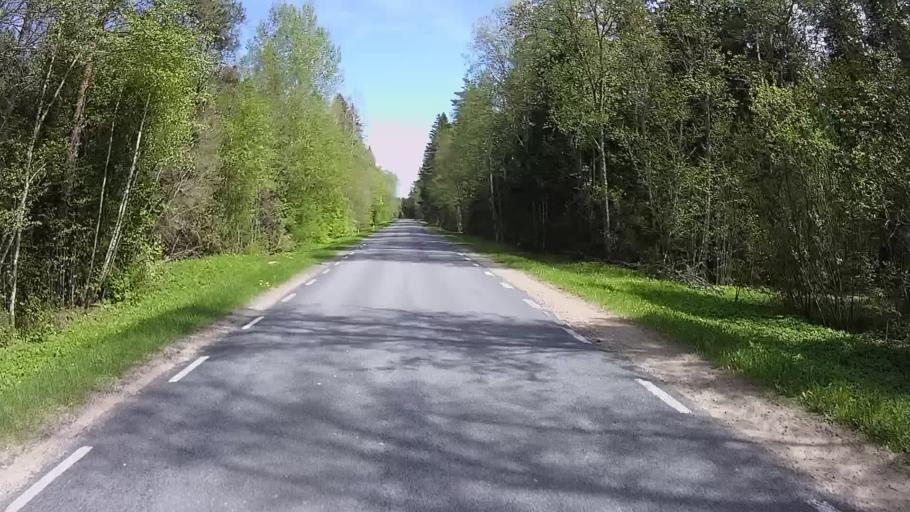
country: LV
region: Apes Novads
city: Ape
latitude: 57.6030
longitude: 26.5159
